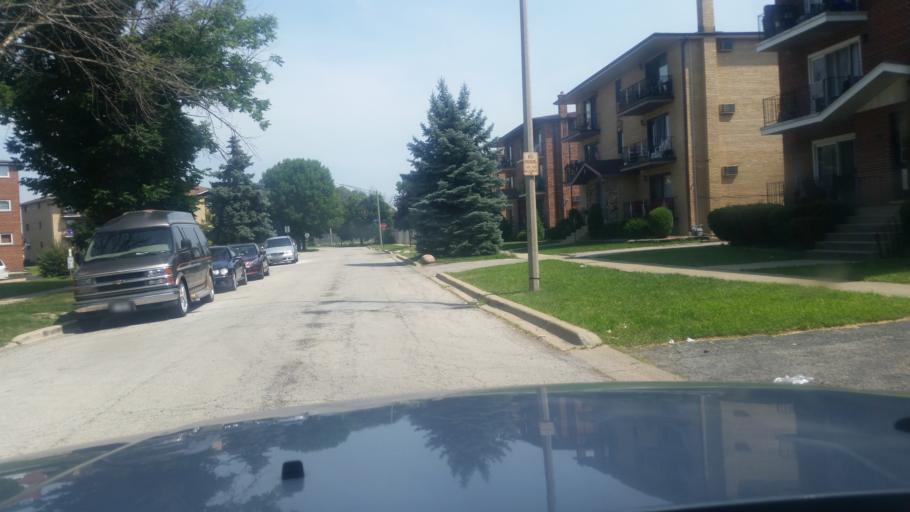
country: US
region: Illinois
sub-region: Cook County
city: Oak Lawn
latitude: 41.6986
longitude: -87.7633
